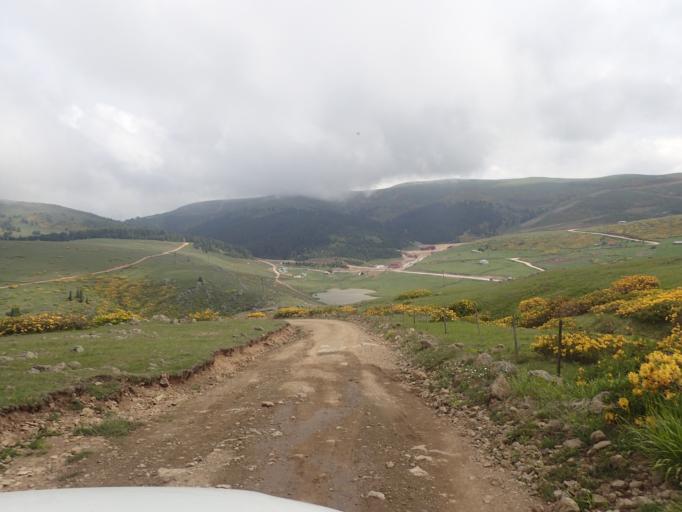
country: TR
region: Ordu
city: Topcam
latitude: 40.6444
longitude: 37.9392
